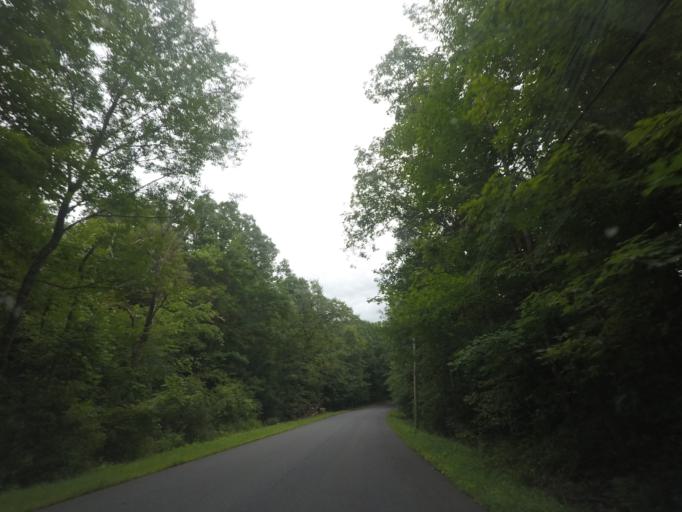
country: US
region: New York
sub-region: Rensselaer County
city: Nassau
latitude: 42.4878
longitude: -73.5971
